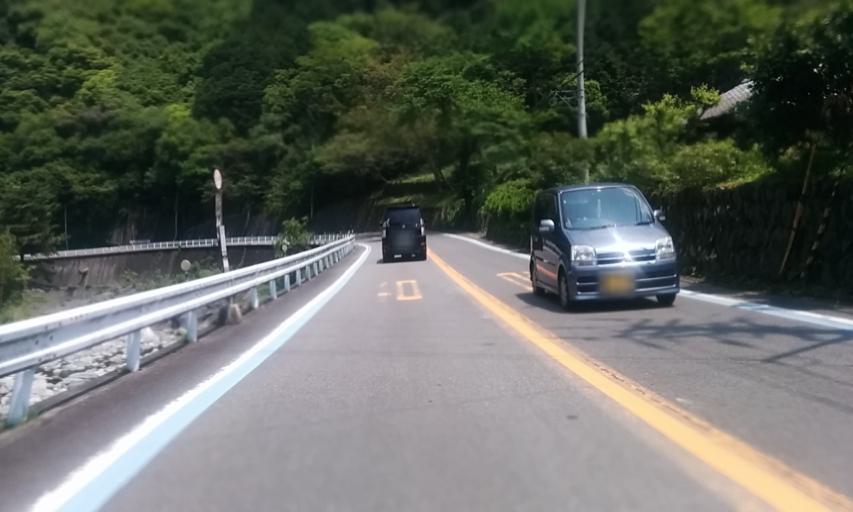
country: JP
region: Ehime
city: Niihama
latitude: 33.9163
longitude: 133.3122
